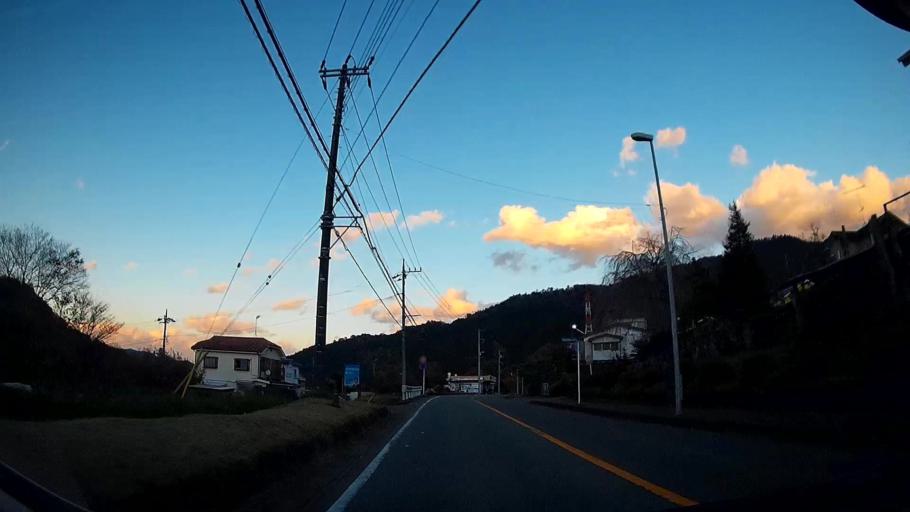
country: JP
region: Yamanashi
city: Uenohara
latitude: 35.5648
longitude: 139.2119
